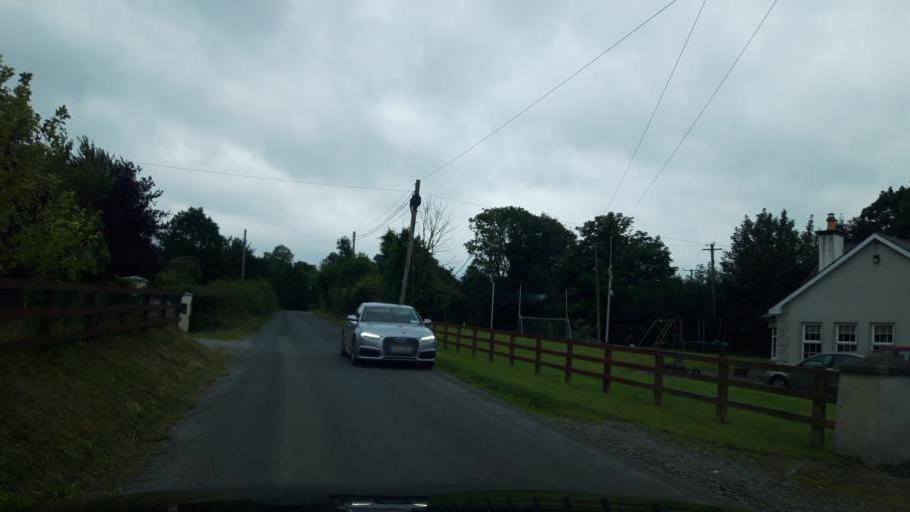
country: IE
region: Leinster
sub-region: Kilkenny
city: Ballyragget
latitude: 52.7188
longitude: -7.4030
